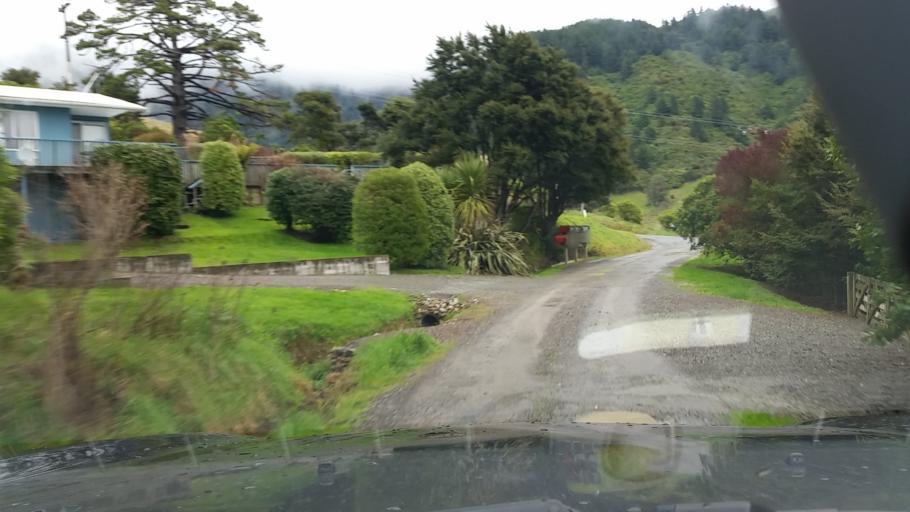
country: NZ
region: Marlborough
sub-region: Marlborough District
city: Picton
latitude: -41.2705
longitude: 174.0768
